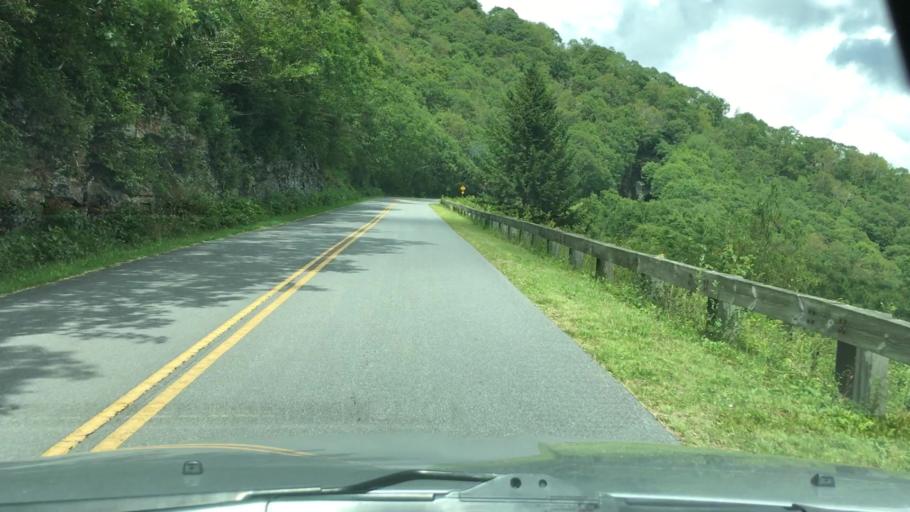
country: US
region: North Carolina
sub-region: Buncombe County
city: Swannanoa
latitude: 35.6844
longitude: -82.3852
